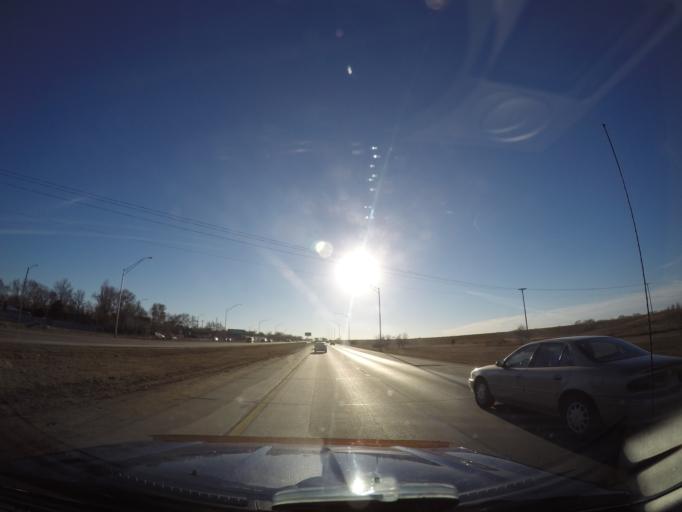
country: US
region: Kansas
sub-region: Sedgwick County
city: Wichita
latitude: 37.7236
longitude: -97.3885
